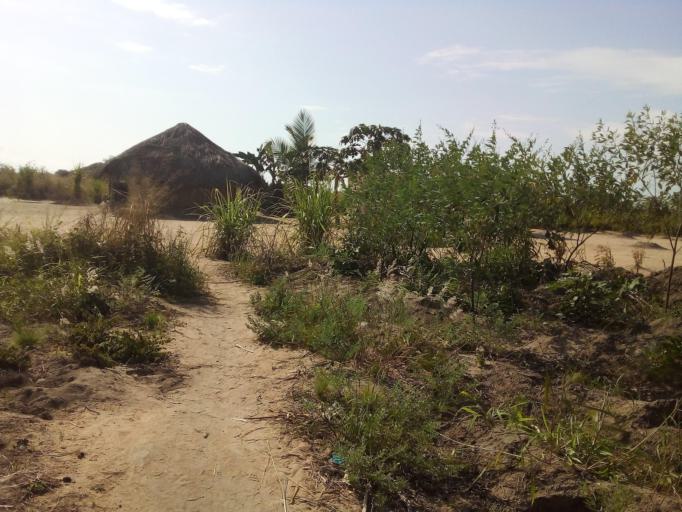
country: MZ
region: Zambezia
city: Quelimane
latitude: -17.5531
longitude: 36.7063
